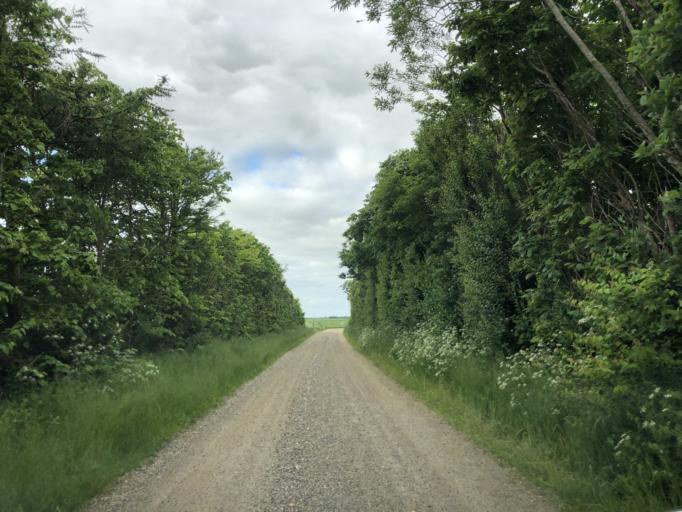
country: DK
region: Central Jutland
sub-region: Holstebro Kommune
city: Ulfborg
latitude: 56.2291
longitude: 8.1939
